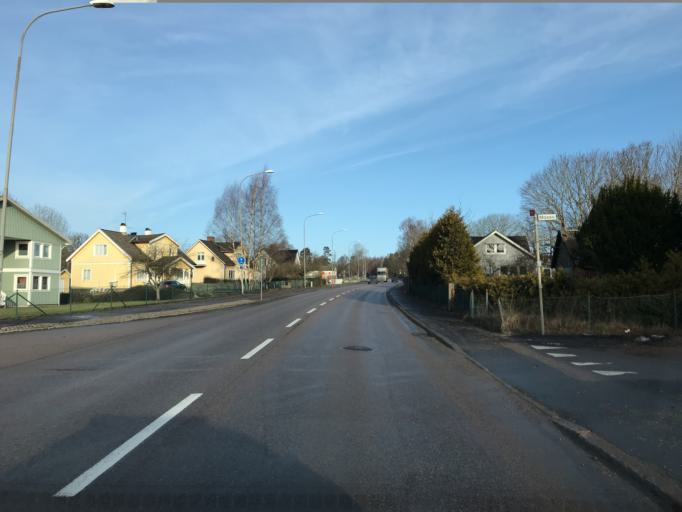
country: SE
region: Skane
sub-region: Hassleholms Kommun
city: Bjarnum
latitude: 56.2940
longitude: 13.7085
